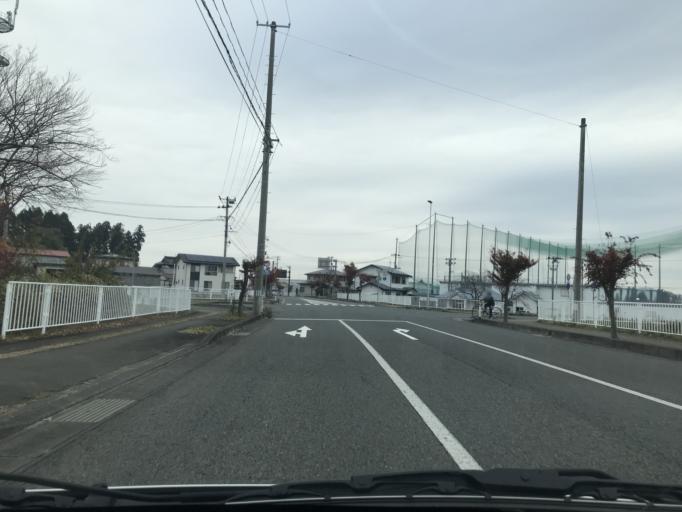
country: JP
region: Iwate
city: Mizusawa
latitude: 39.1187
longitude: 141.1224
